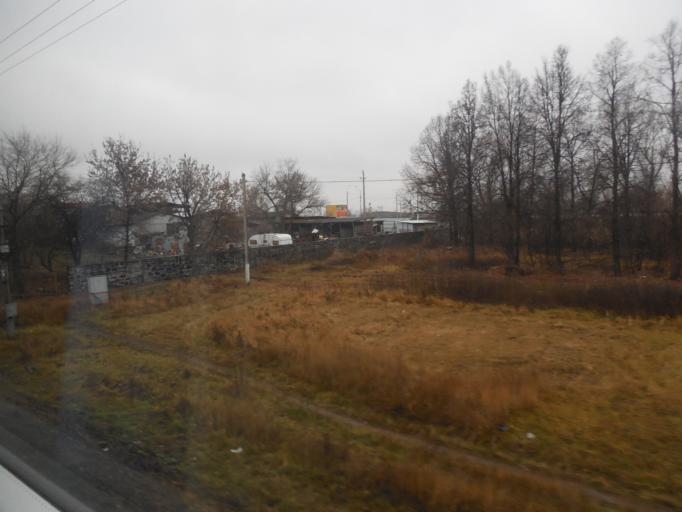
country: RU
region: Moskovskaya
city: Yam
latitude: 55.4707
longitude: 37.7511
